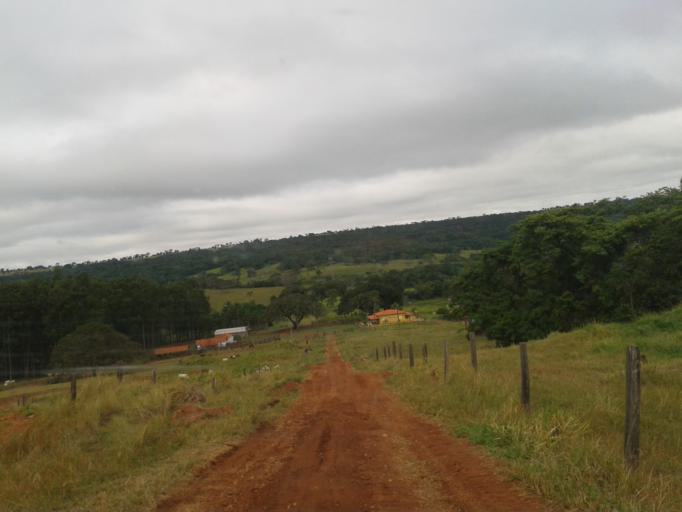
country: BR
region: Minas Gerais
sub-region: Campina Verde
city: Campina Verde
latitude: -19.4245
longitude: -49.6468
